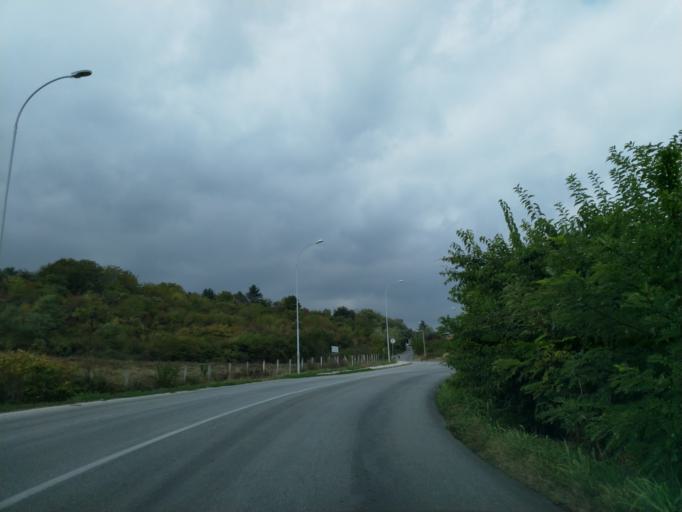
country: RS
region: Central Serbia
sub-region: Pomoravski Okrug
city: Jagodina
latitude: 43.9873
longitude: 21.2374
